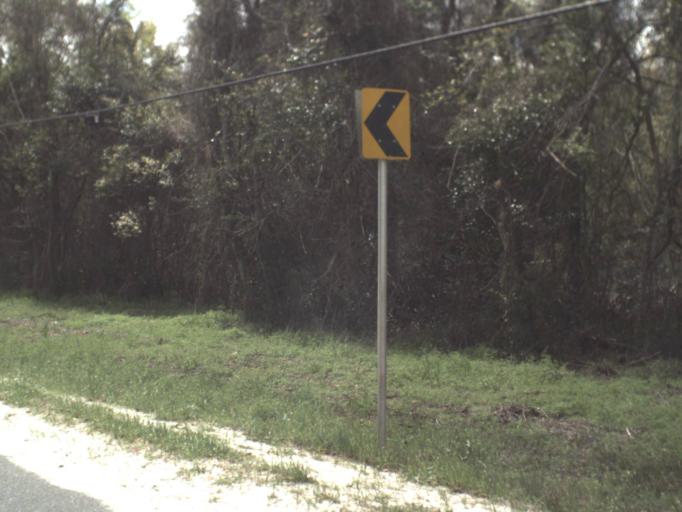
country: US
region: Florida
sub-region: Wakulla County
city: Crawfordville
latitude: 30.1464
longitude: -84.3878
